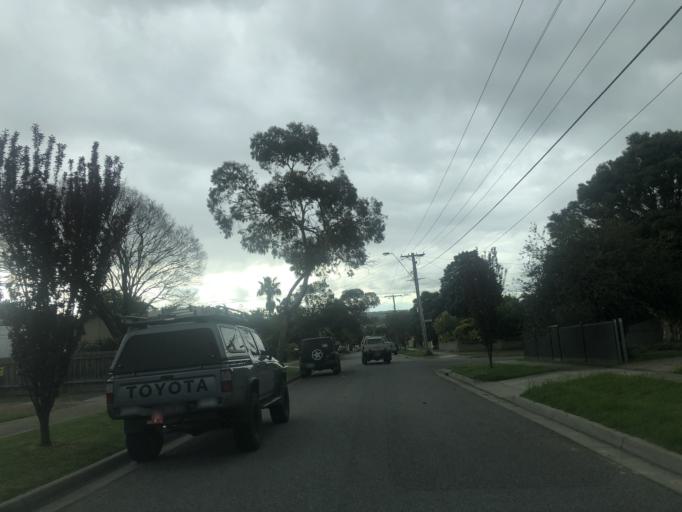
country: AU
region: Victoria
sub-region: Casey
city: Doveton
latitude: -37.9866
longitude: 145.2469
